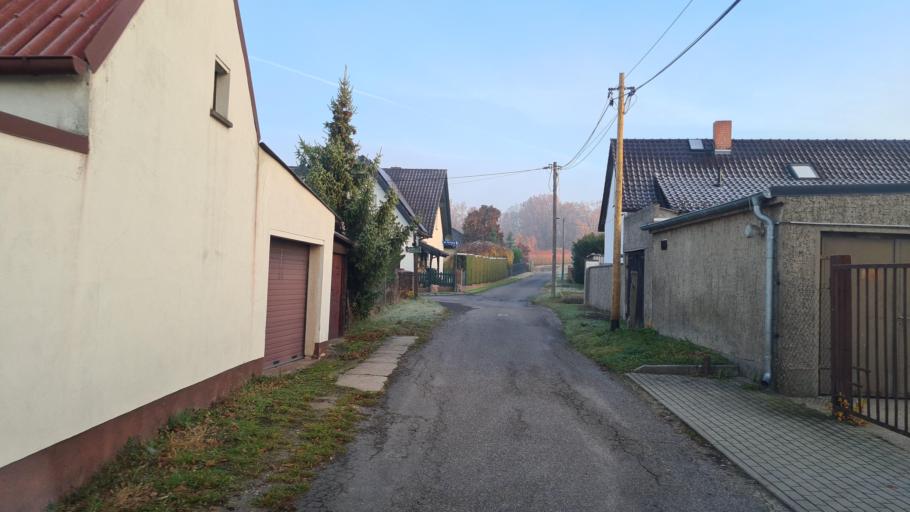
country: DE
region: Saxony-Anhalt
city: Jessen
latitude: 51.7977
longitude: 12.9855
